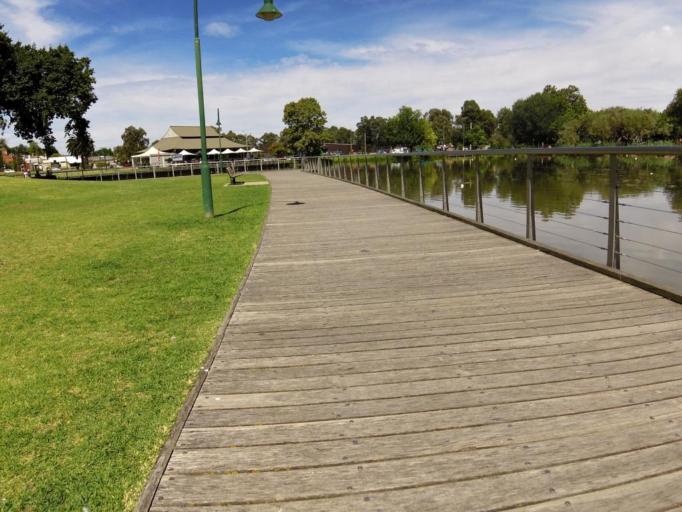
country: AU
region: Victoria
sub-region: Greater Bendigo
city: Bendigo
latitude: -36.7480
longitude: 144.2911
